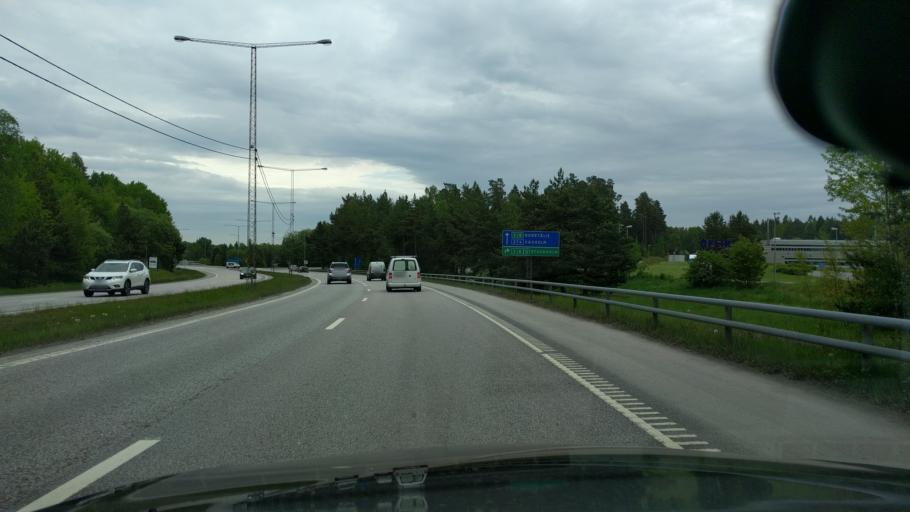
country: SE
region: Stockholm
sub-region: Taby Kommun
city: Taby
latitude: 59.4585
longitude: 18.1316
